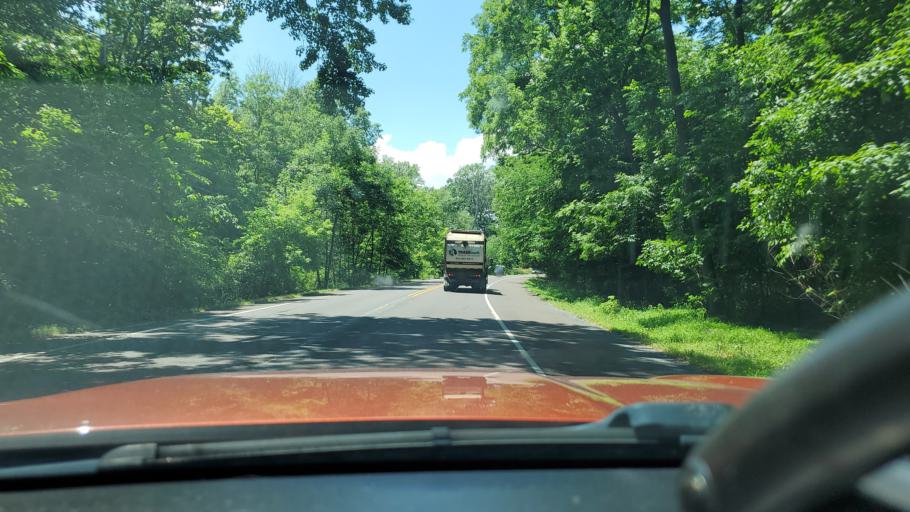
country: US
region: Pennsylvania
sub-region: Montgomery County
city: Gilbertsville
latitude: 40.3155
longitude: -75.5822
